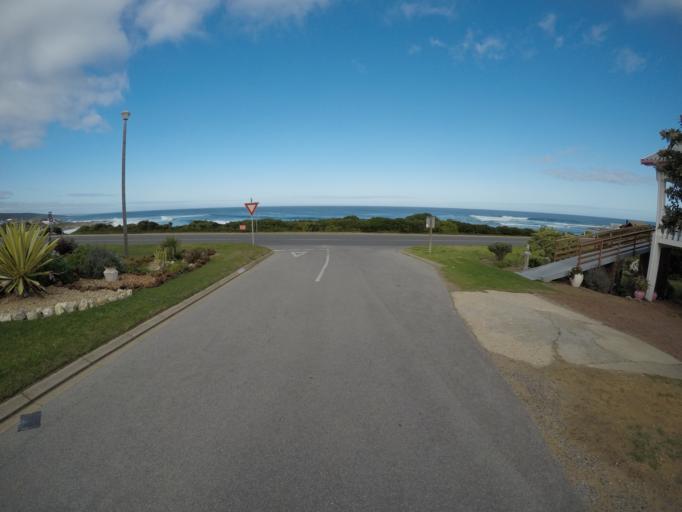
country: ZA
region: Western Cape
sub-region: Eden District Municipality
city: Riversdale
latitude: -34.4276
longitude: 21.3355
